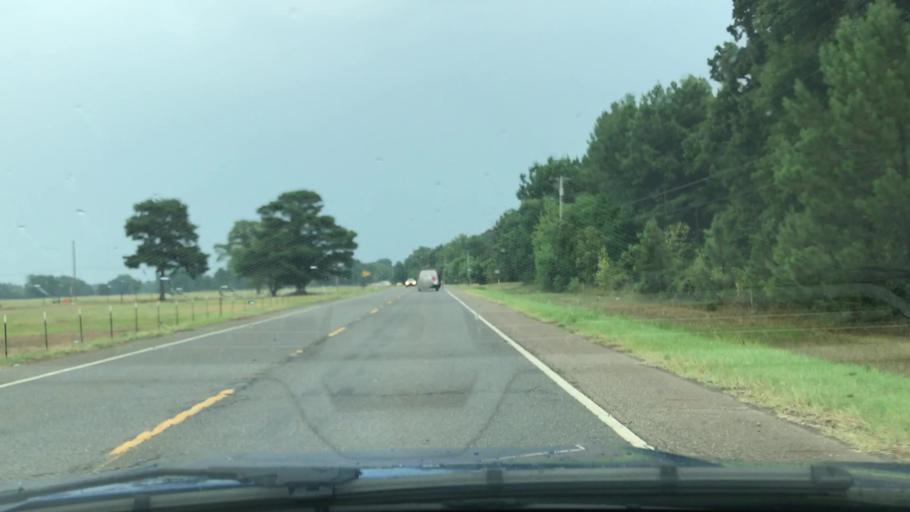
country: US
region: Texas
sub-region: Harrison County
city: Waskom
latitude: 32.4639
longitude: -94.0323
